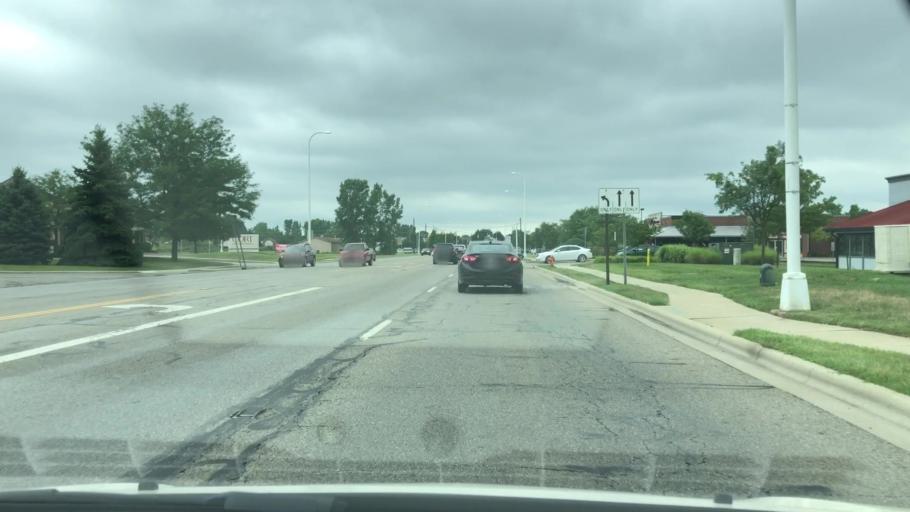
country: US
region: Ohio
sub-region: Franklin County
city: Worthington
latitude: 40.1399
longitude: -82.9917
